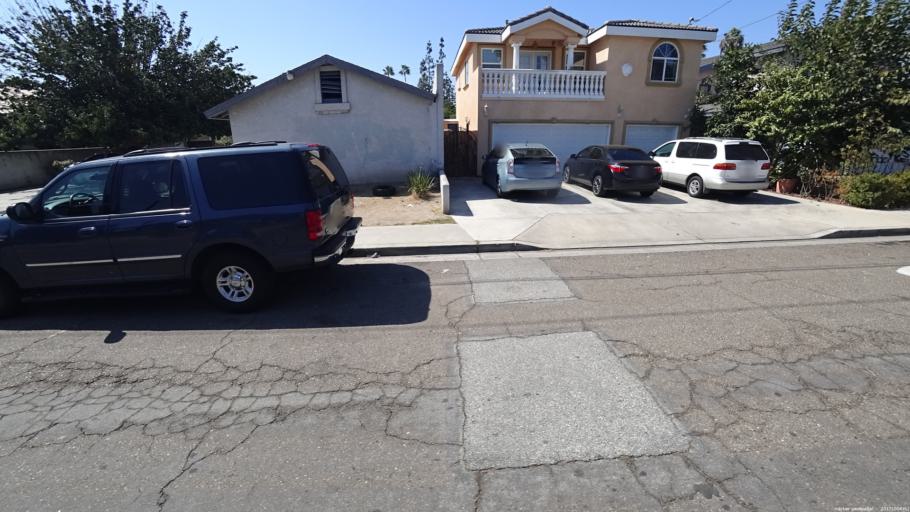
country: US
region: California
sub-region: Orange County
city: Garden Grove
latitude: 33.7716
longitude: -117.9446
